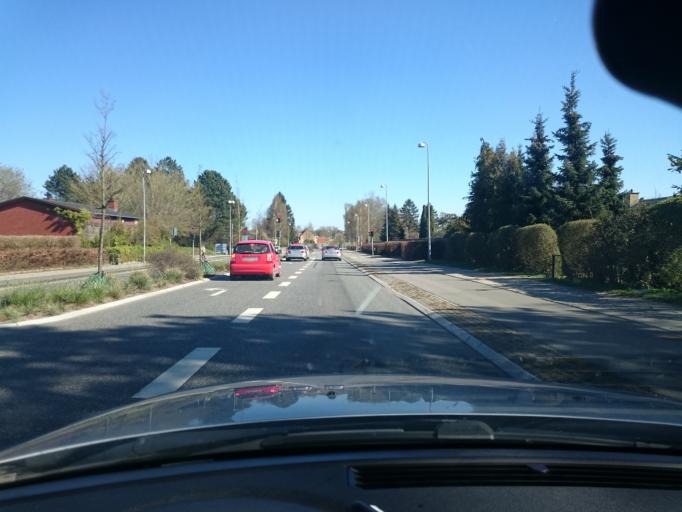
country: DK
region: Capital Region
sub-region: Fureso Kommune
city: Vaerlose
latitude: 55.7812
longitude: 12.3741
